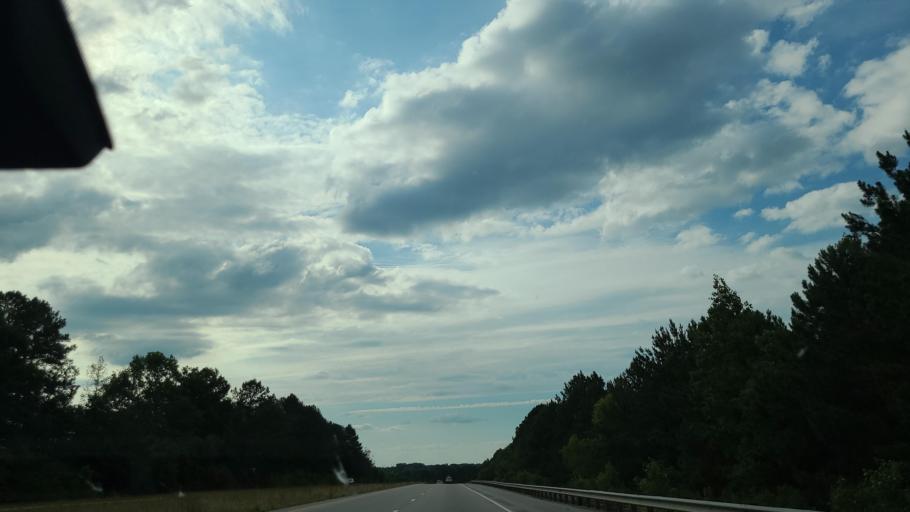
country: US
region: Georgia
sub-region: Putnam County
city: Eatonton
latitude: 33.3128
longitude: -83.4024
